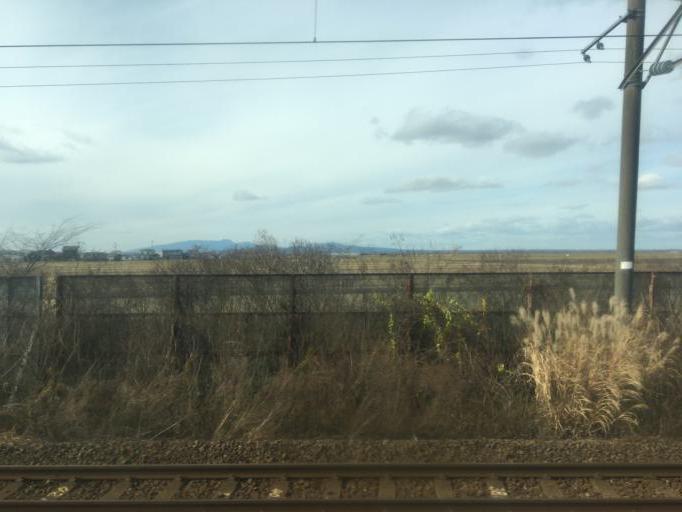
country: JP
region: Akita
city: Tenno
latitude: 39.9017
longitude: 140.0743
